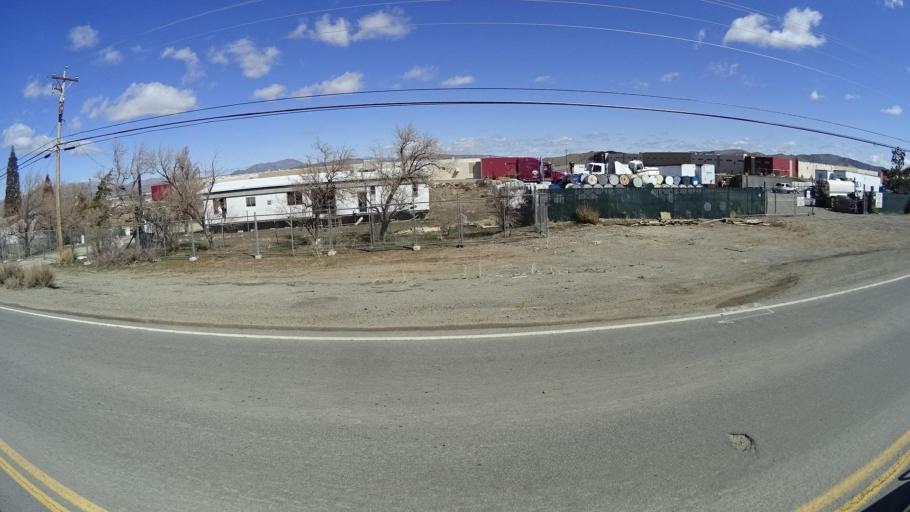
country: US
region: Nevada
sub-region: Washoe County
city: Lemmon Valley
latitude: 39.6118
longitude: -119.8724
